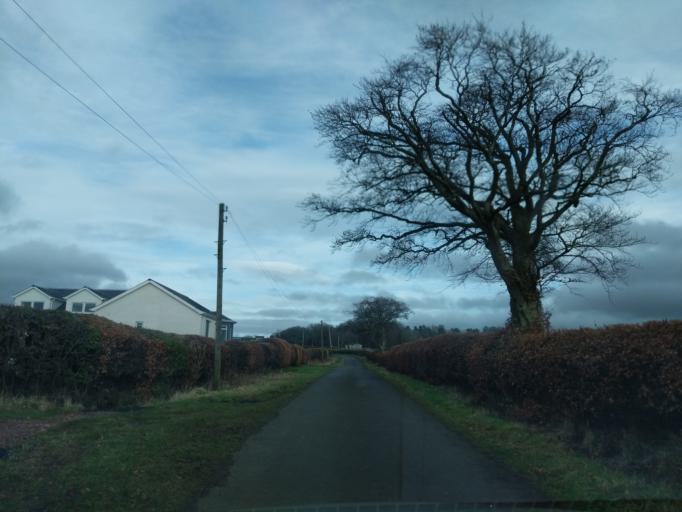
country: GB
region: Scotland
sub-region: South Lanarkshire
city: Carluke
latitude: 55.7097
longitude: -3.8553
